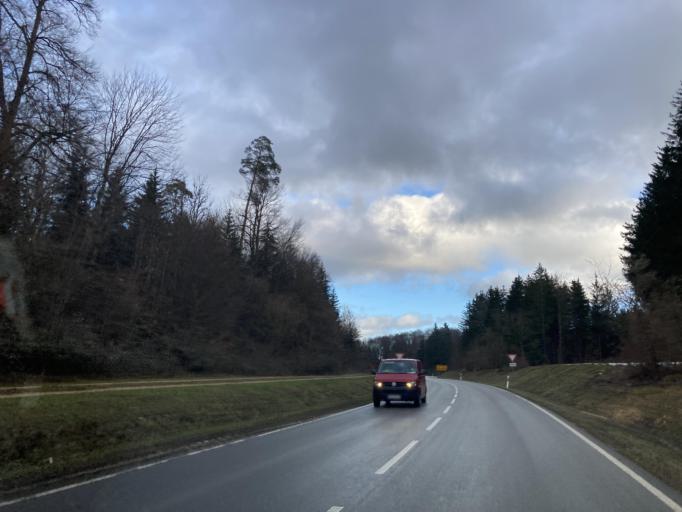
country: DE
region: Baden-Wuerttemberg
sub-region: Freiburg Region
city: Neuhausen ob Eck
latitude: 47.9761
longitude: 8.9526
